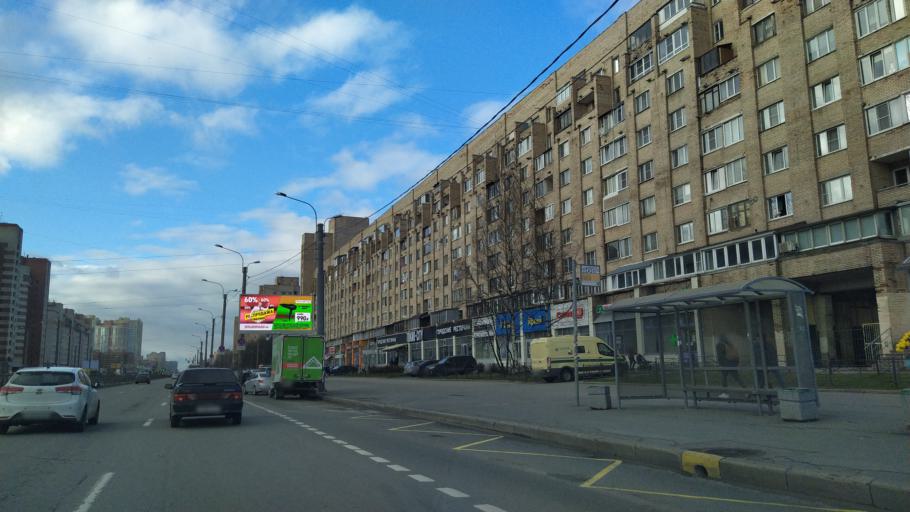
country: RU
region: St.-Petersburg
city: Grazhdanka
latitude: 60.0426
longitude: 30.3860
